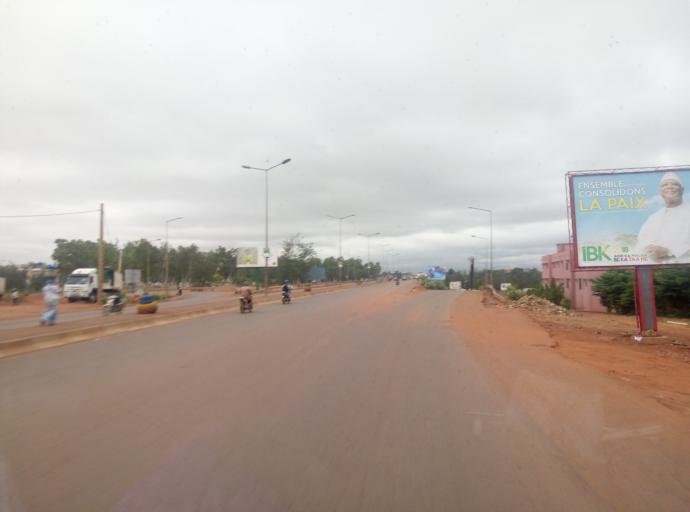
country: ML
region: Bamako
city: Bamako
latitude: 12.6105
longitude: -7.9953
